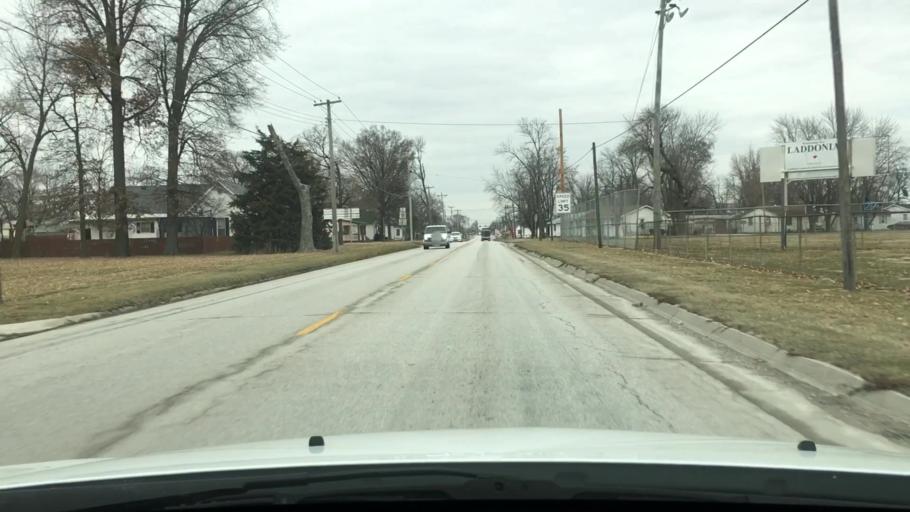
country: US
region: Missouri
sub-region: Audrain County
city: Vandalia
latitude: 39.2372
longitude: -91.6457
